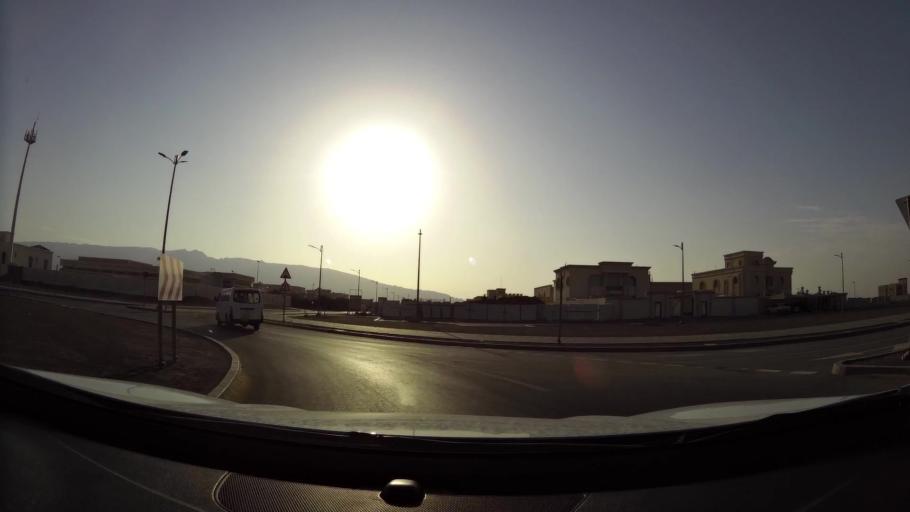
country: AE
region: Abu Dhabi
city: Al Ain
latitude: 24.1092
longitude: 55.8397
